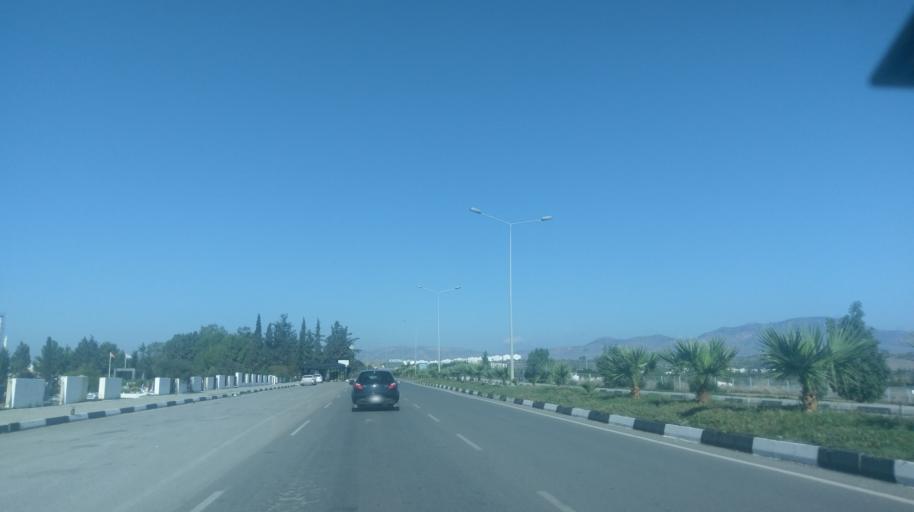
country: CY
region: Lefkosia
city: Nicosia
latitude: 35.2176
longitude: 33.3319
